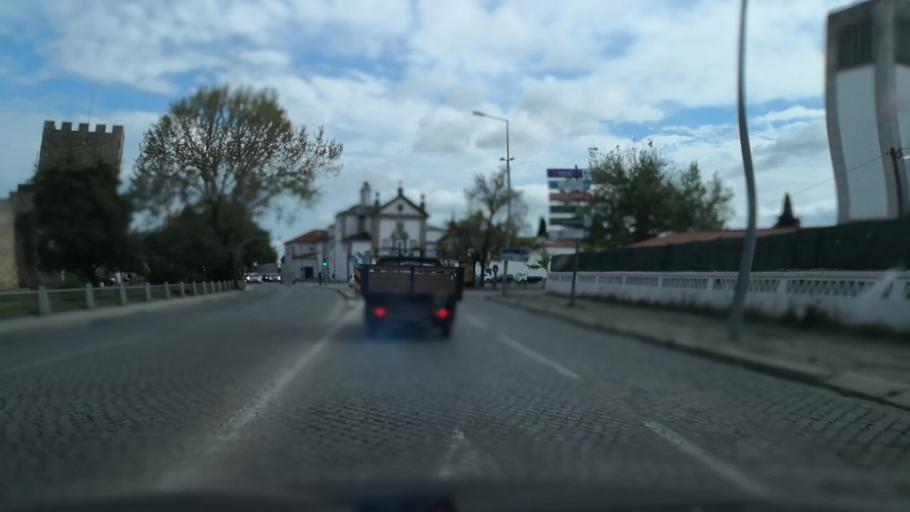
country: PT
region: Evora
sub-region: Evora
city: Evora
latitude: 38.5711
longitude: -7.9151
